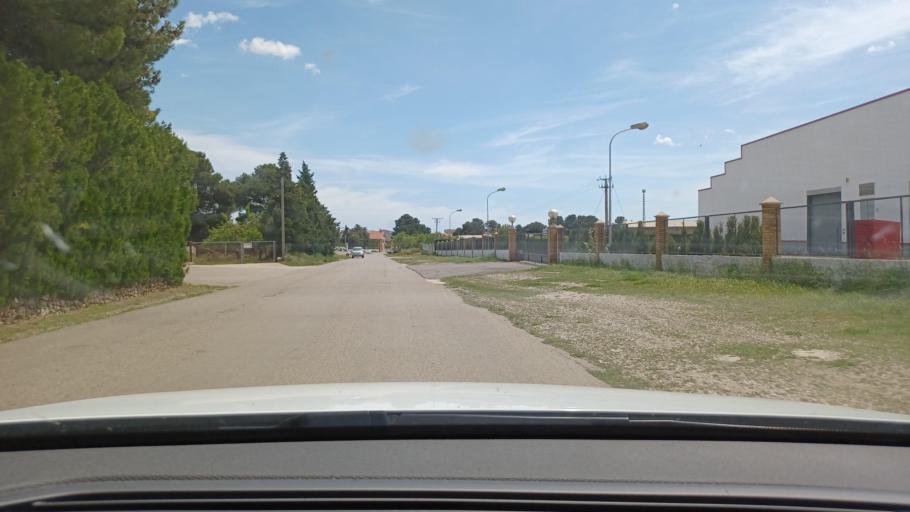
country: ES
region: Valencia
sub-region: Provincia de Castello
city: Rosell
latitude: 40.6420
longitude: 0.2757
